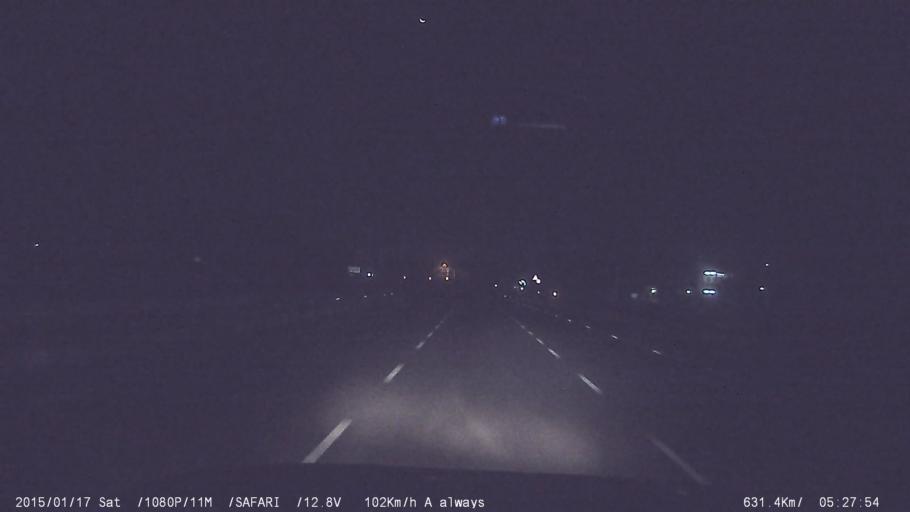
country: IN
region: Tamil Nadu
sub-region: Vellore
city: Arcot
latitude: 12.9273
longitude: 79.2644
